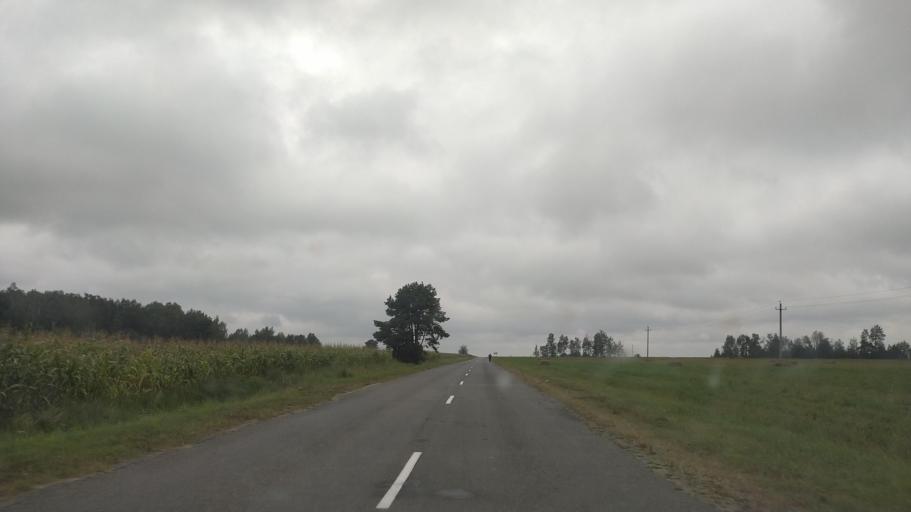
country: BY
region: Brest
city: Byaroza
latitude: 52.5630
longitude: 24.9052
